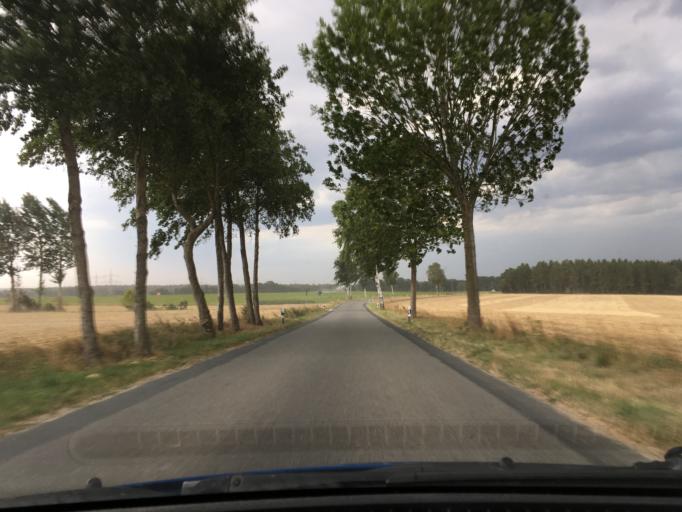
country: DE
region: Lower Saxony
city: Hanstedt Eins
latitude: 53.0640
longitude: 10.3840
